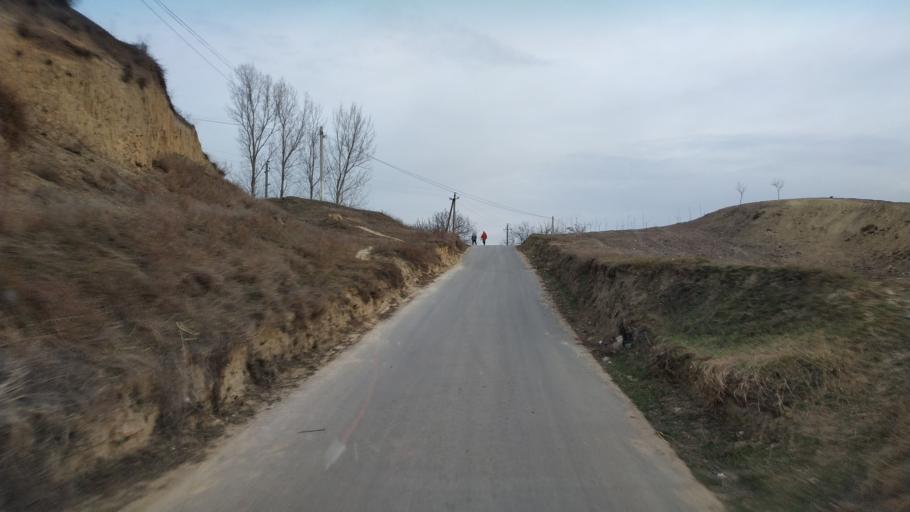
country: MD
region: Hincesti
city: Dancu
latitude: 46.7481
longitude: 28.2085
